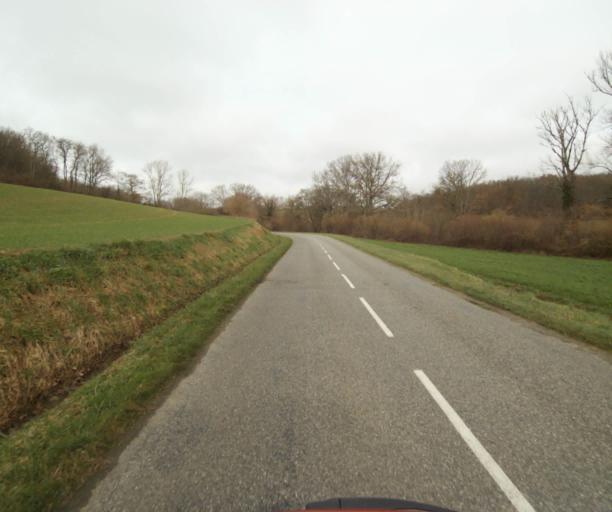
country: FR
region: Midi-Pyrenees
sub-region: Departement de l'Ariege
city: Pamiers
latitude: 43.1452
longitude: 1.5286
